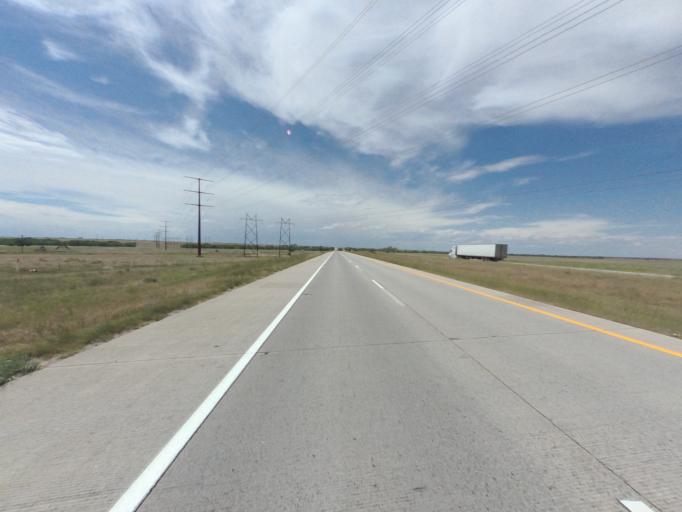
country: US
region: Colorado
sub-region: Arapahoe County
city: Byers
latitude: 39.6666
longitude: -104.0902
